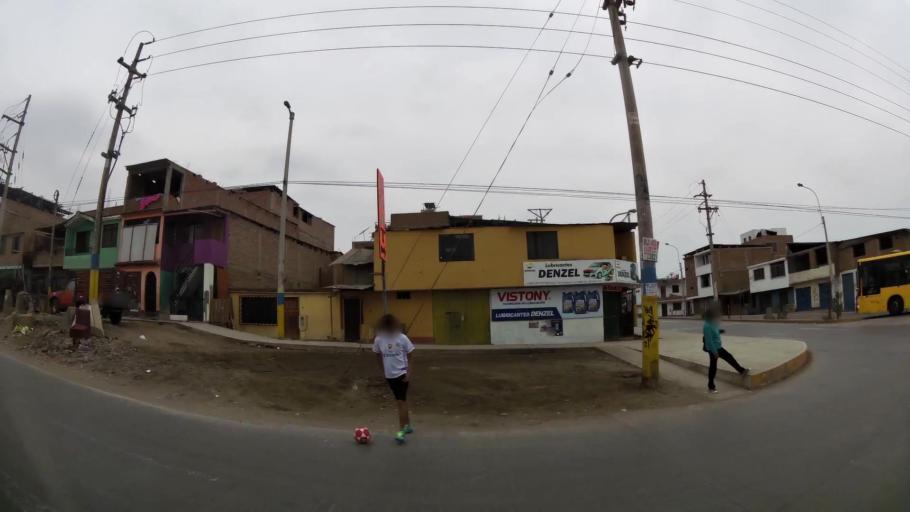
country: PE
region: Lima
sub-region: Lima
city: Surco
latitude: -12.2021
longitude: -76.9465
